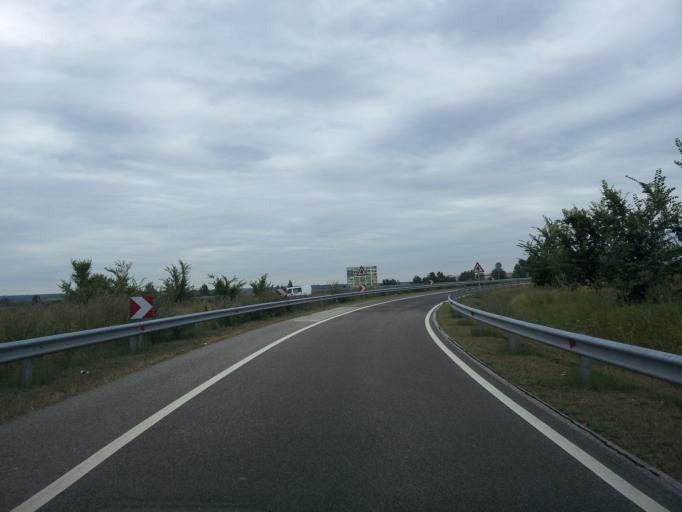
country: HU
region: Pest
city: Tarnok
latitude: 47.3769
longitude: 18.8324
